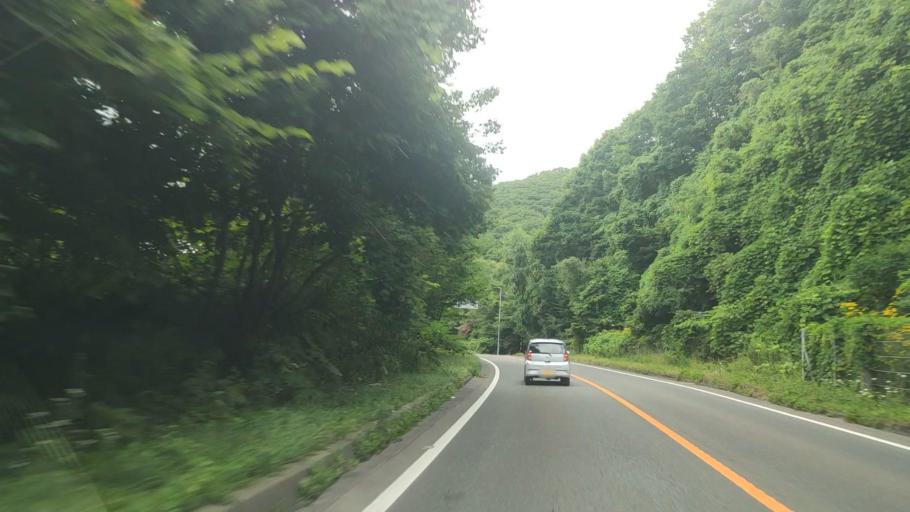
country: JP
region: Hokkaido
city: Date
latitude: 42.5663
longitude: 140.7364
